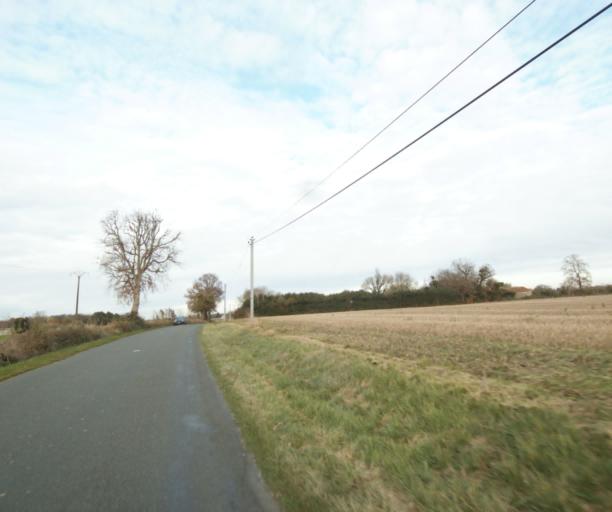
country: FR
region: Poitou-Charentes
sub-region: Departement de la Charente-Maritime
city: Corme-Royal
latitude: 45.7513
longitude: -0.8055
